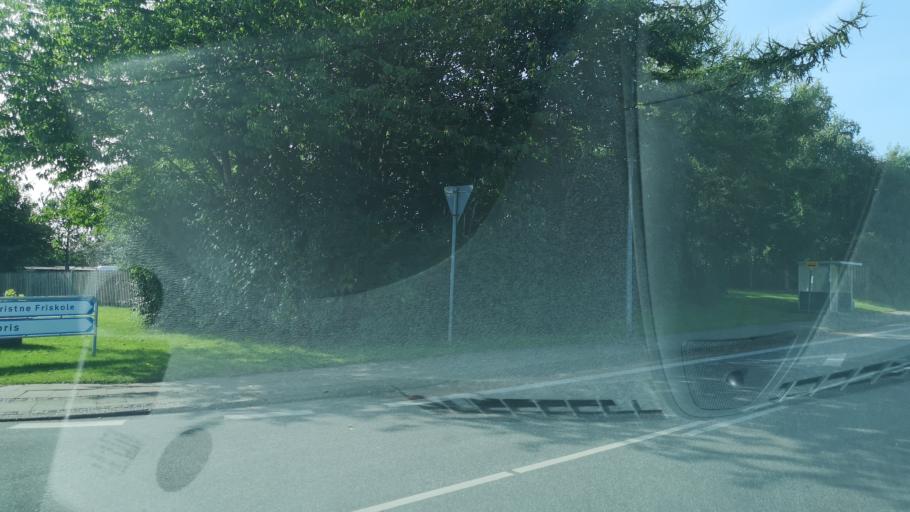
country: DK
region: Central Jutland
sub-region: Ringkobing-Skjern Kommune
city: Videbaek
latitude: 56.0848
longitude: 8.6281
